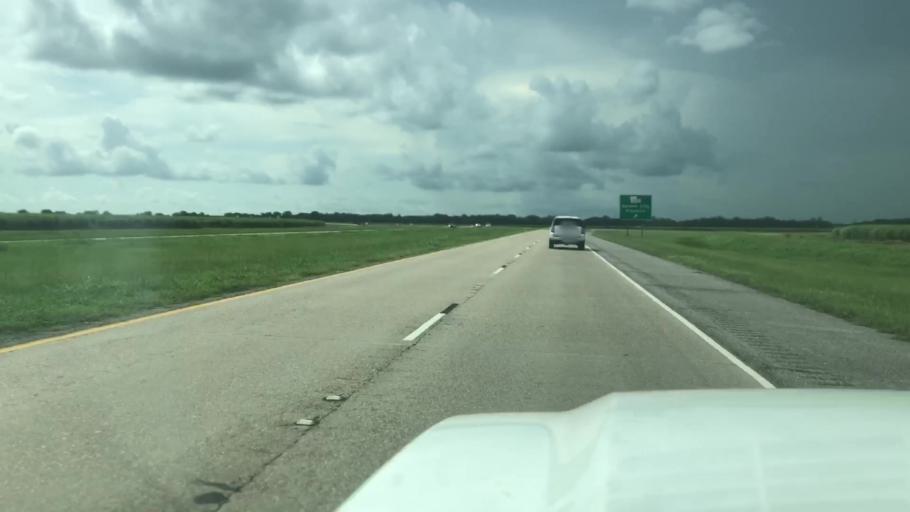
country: US
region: Louisiana
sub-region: Saint Mary Parish
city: Franklin
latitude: 29.7549
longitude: -91.4527
